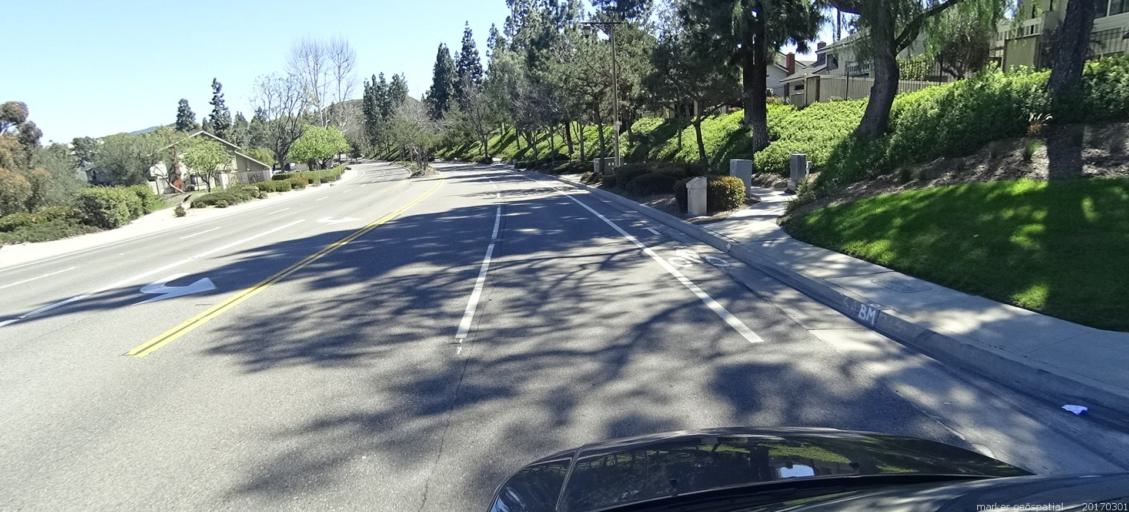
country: US
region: California
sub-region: Orange County
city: Villa Park
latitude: 33.8463
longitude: -117.7548
